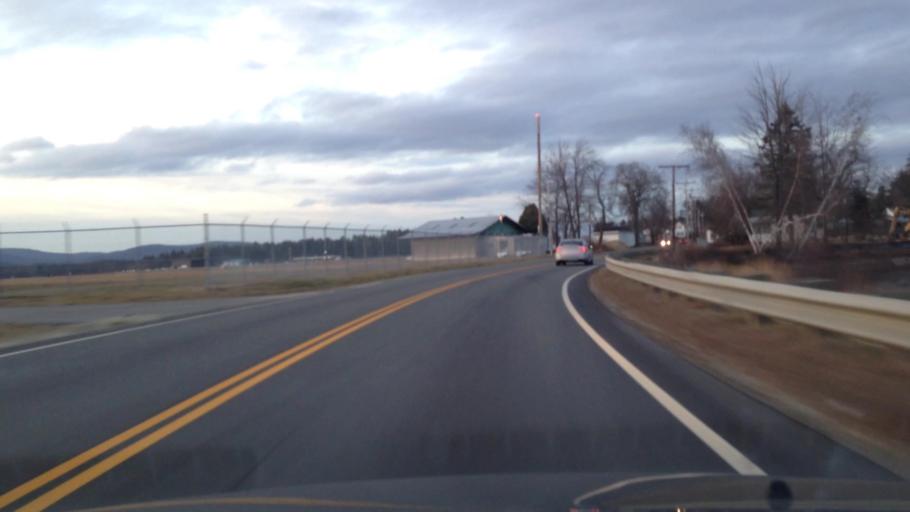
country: US
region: New Hampshire
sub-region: Cheshire County
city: Swanzey
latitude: 42.8987
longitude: -72.2641
